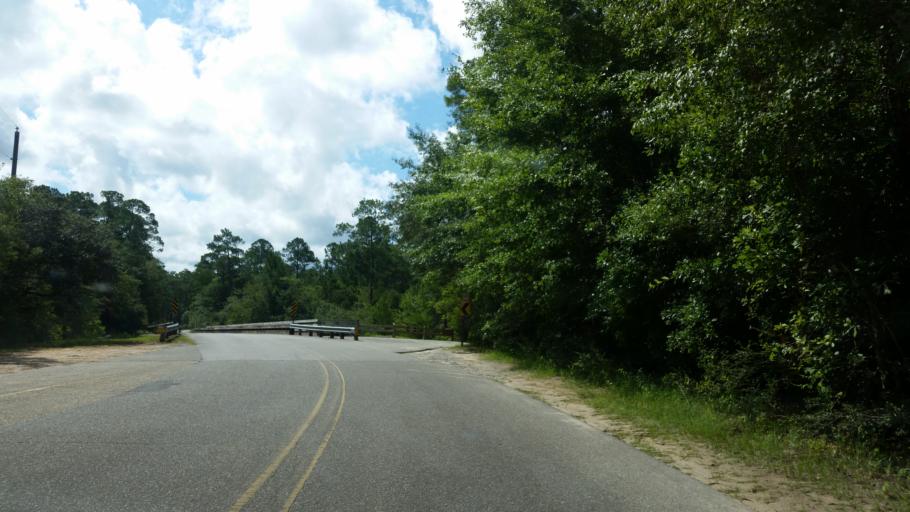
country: US
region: Florida
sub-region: Santa Rosa County
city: East Milton
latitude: 30.7052
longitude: -86.8825
